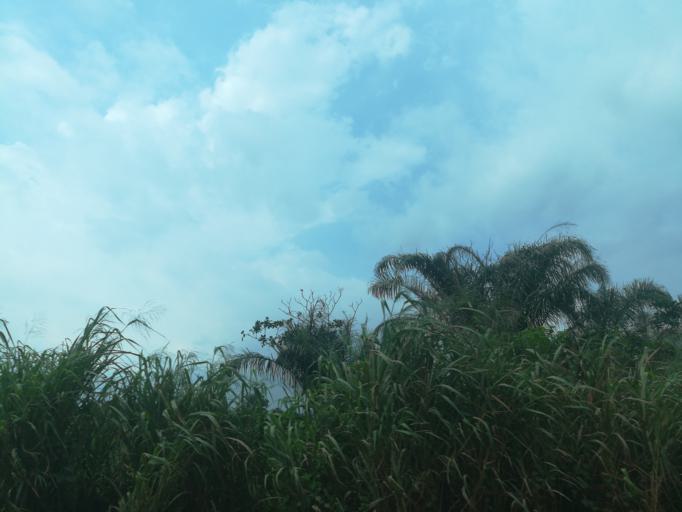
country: NG
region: Lagos
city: Ikorodu
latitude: 6.6717
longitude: 3.6641
